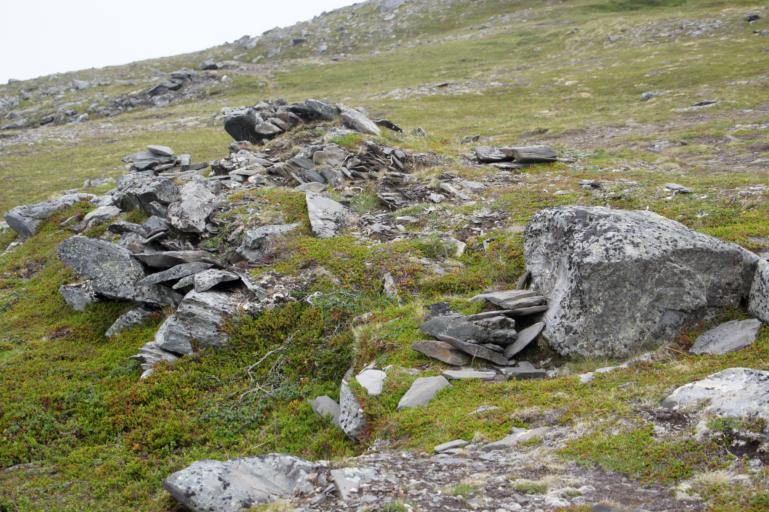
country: NO
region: Finnmark Fylke
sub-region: Nordkapp
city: Honningsvag
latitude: 71.1118
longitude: 25.8022
